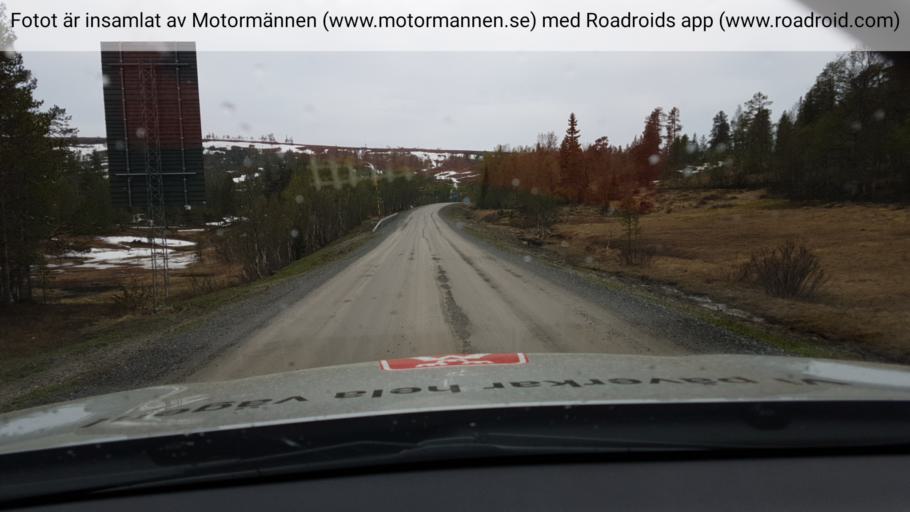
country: NO
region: Nord-Trondelag
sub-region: Snasa
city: Snaase
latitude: 63.6904
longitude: 12.3134
